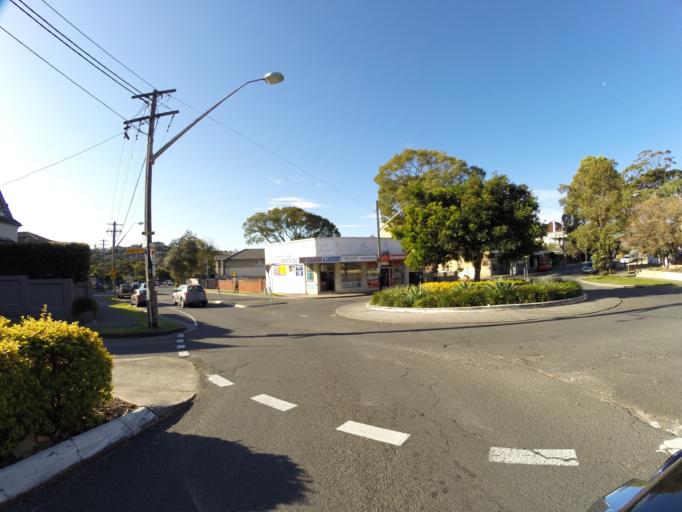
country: AU
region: New South Wales
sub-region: Waverley
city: Bronte
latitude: -33.9030
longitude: 151.2597
